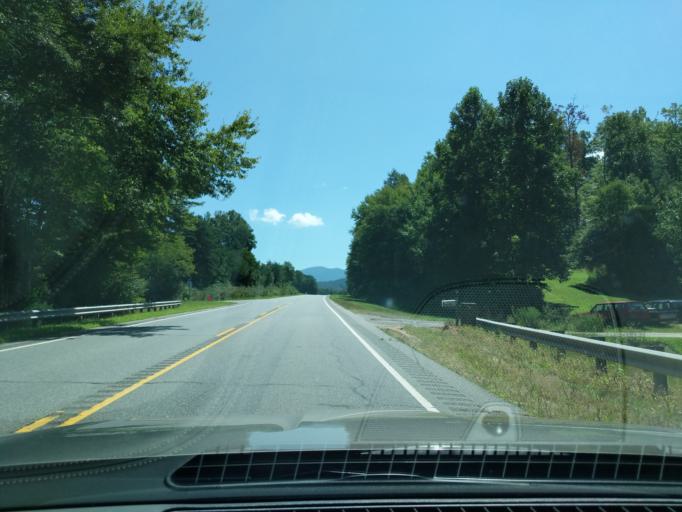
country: US
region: Georgia
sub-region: Towns County
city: Hiawassee
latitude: 35.0305
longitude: -83.7270
